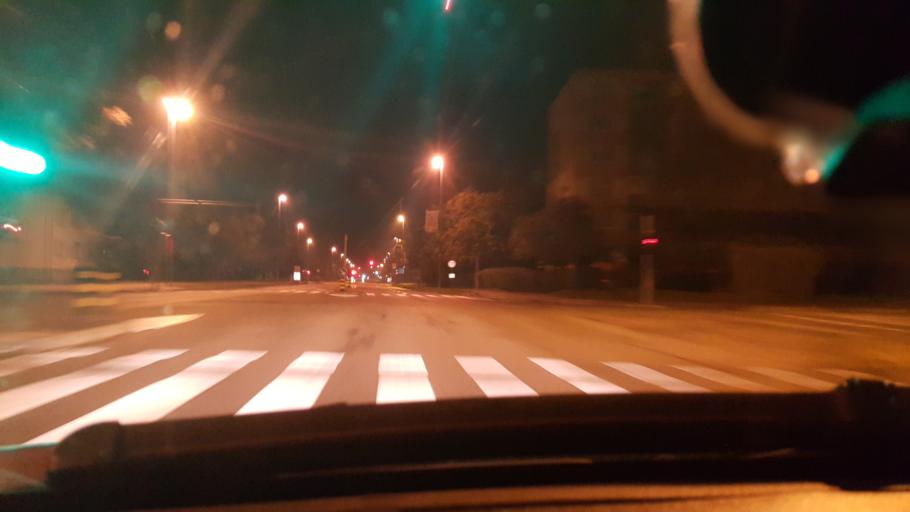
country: SI
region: Maribor
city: Maribor
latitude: 46.5418
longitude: 15.6377
